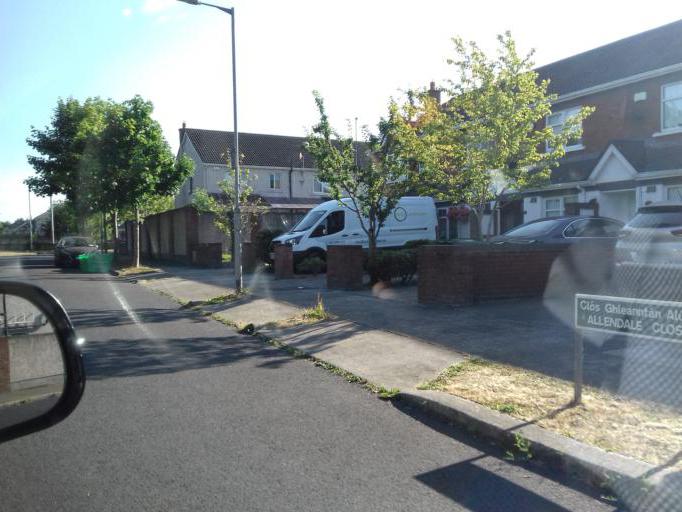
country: IE
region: Leinster
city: Hartstown
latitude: 53.3907
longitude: -6.4255
